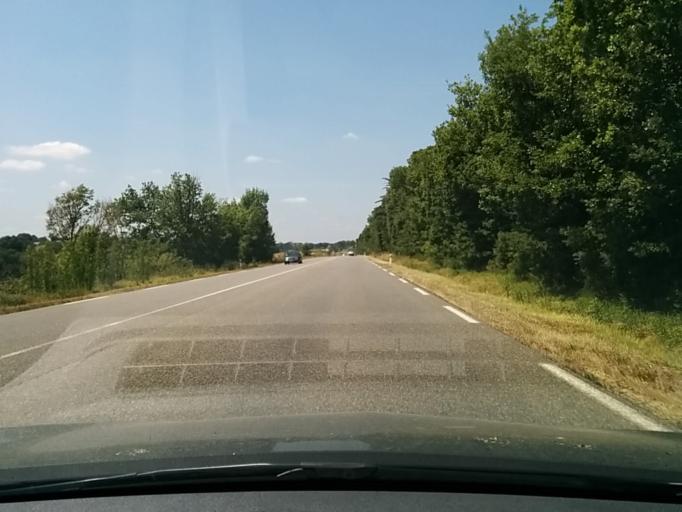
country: FR
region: Midi-Pyrenees
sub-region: Departement du Gers
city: Gimont
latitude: 43.6356
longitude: 0.8391
